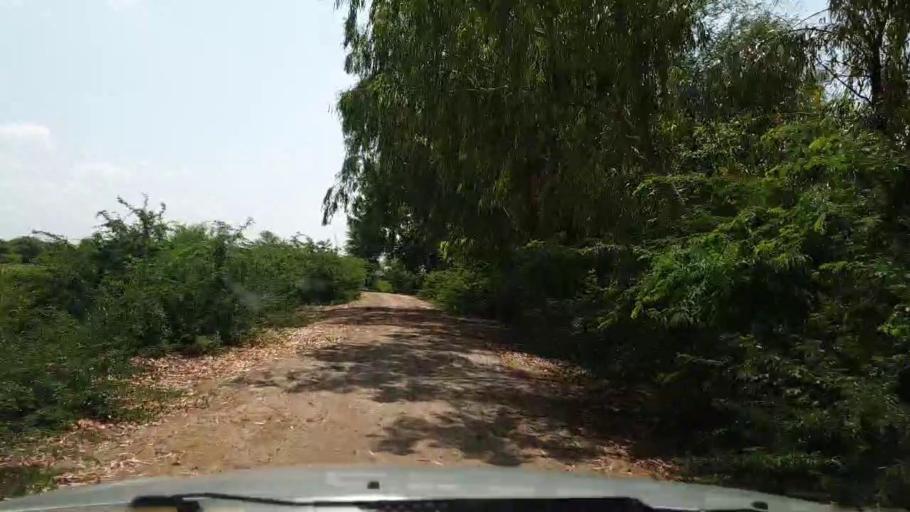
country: PK
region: Sindh
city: Rajo Khanani
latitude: 25.0087
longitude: 68.8578
